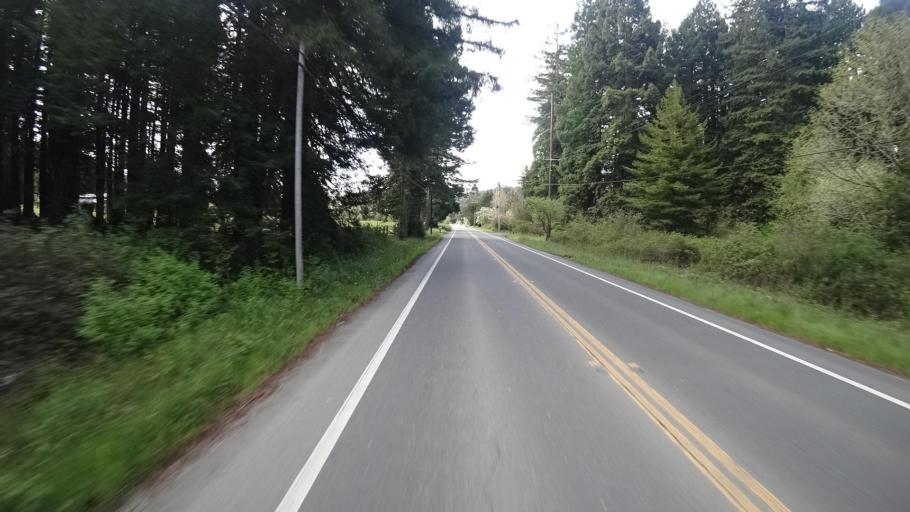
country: US
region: California
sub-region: Humboldt County
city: Myrtletown
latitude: 40.7746
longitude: -124.0735
